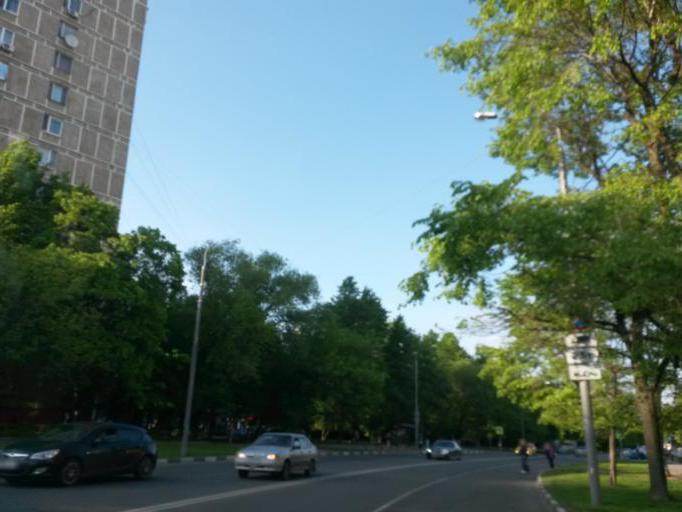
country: RU
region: Moskovskaya
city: Biryulevo Zapadnoye
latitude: 55.5906
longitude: 37.6462
